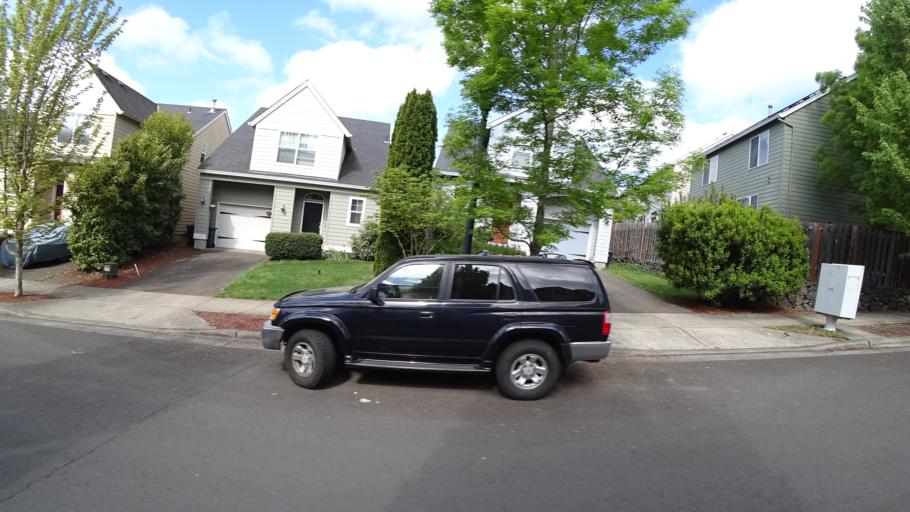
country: US
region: Oregon
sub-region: Washington County
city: Rockcreek
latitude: 45.5216
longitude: -122.8908
